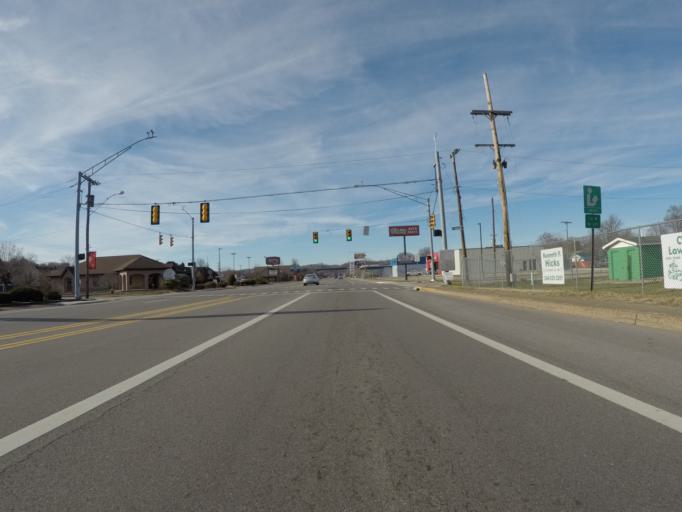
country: US
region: West Virginia
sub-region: Wayne County
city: Kenova
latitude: 38.3986
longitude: -82.5691
